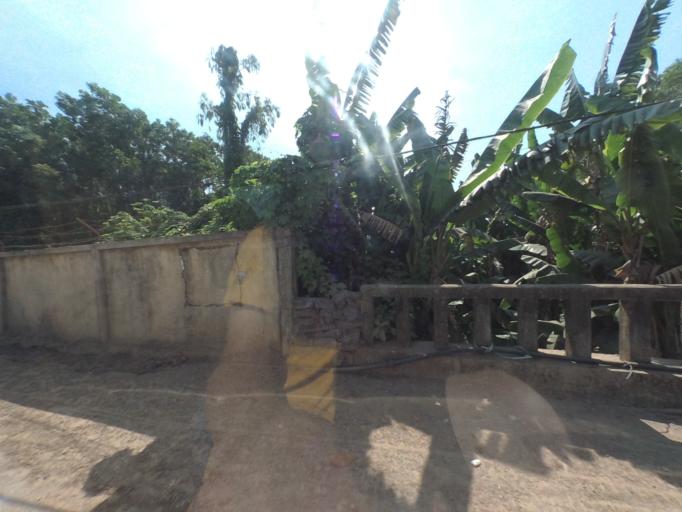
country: VN
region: Da Nang
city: Lien Chieu
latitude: 16.0468
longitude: 108.1426
